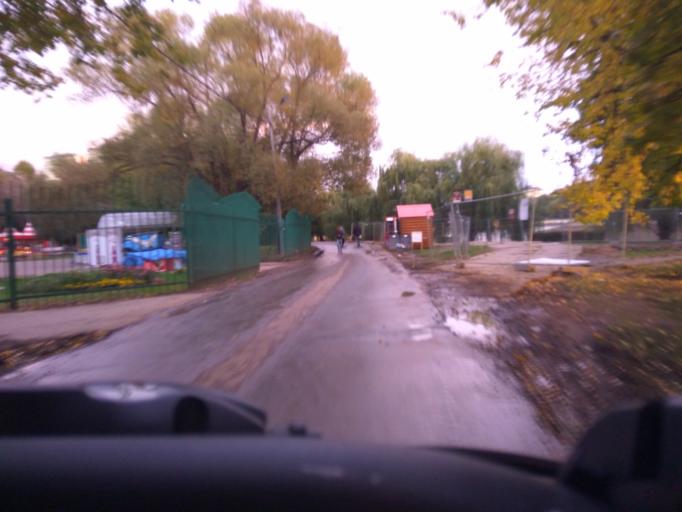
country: RU
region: Moskovskaya
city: Levoberezhnyy
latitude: 55.8547
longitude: 37.4868
